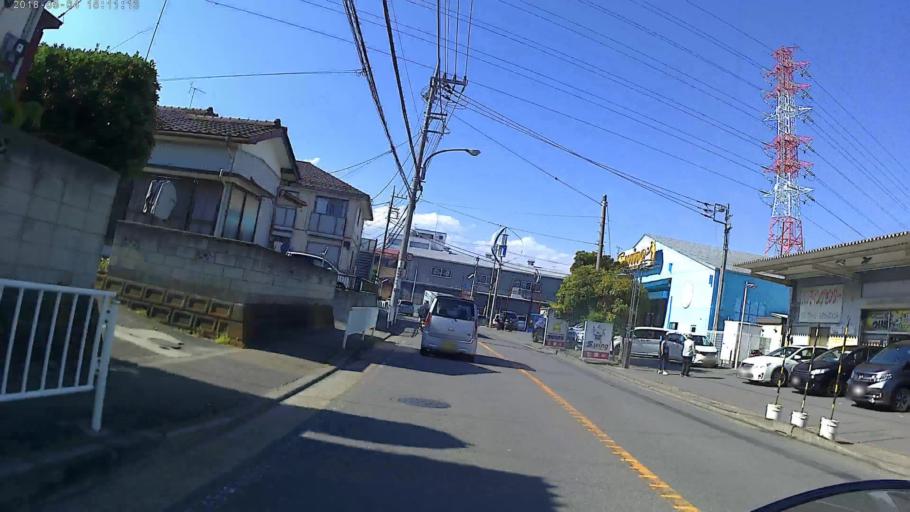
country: JP
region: Kanagawa
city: Yokohama
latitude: 35.5242
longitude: 139.6105
